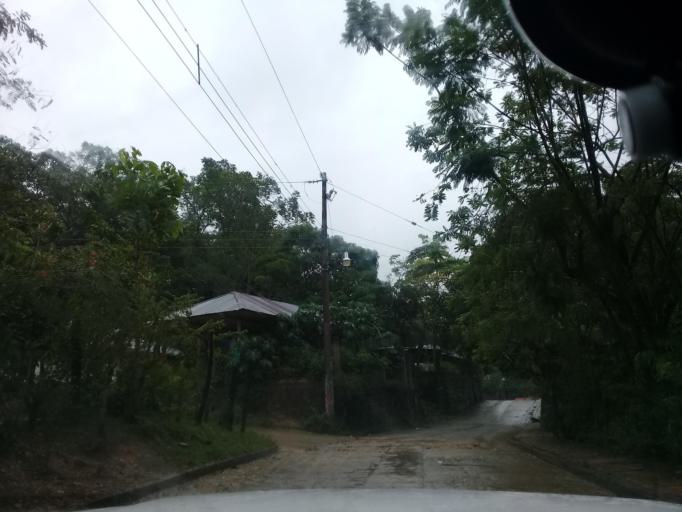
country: MX
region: Veracruz
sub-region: Chalma
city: San Pedro Coyutla
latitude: 21.2323
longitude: -98.4583
